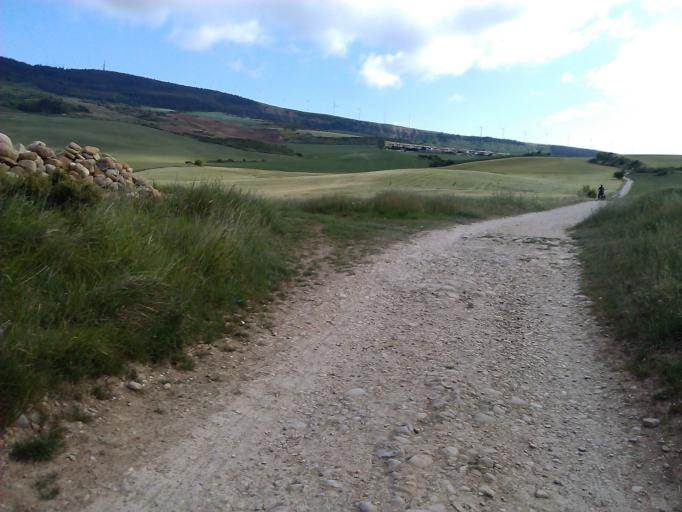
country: ES
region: Navarre
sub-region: Provincia de Navarra
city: Galar
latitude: 42.7566
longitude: -1.7152
